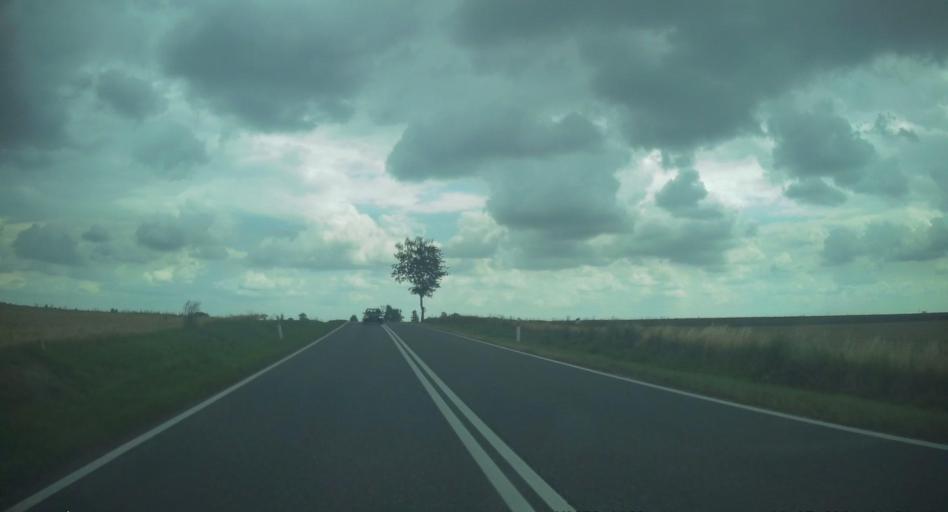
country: PL
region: Opole Voivodeship
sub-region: Powiat prudnicki
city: Moszczanka
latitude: 50.4198
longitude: 17.4712
